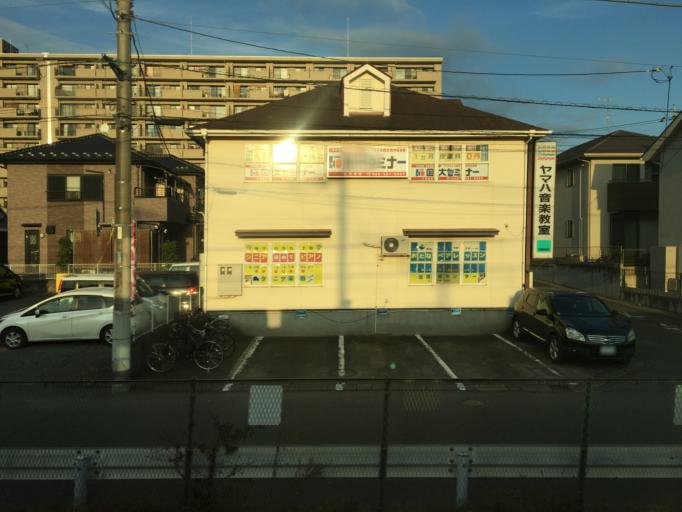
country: JP
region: Saitama
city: Fukiage-fujimi
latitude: 36.0841
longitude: 139.4785
